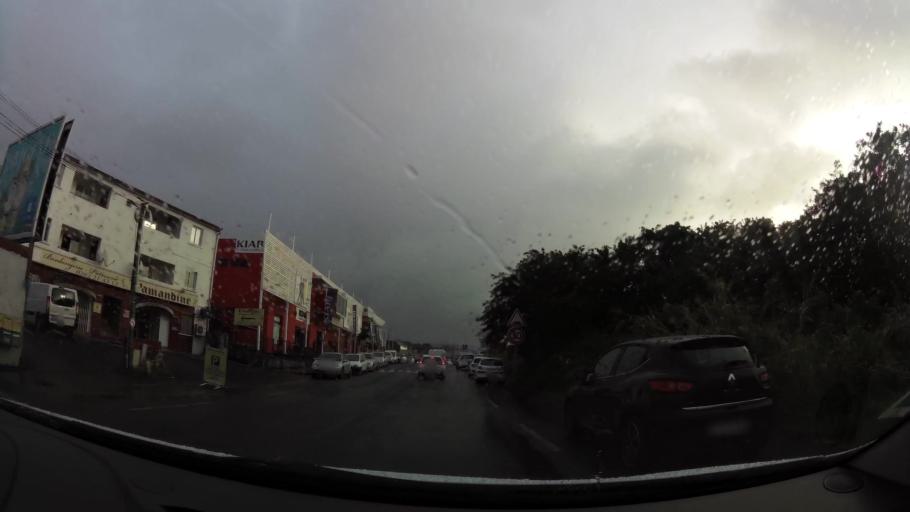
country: RE
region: Reunion
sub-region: Reunion
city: Saint-Andre
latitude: -20.9608
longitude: 55.6620
